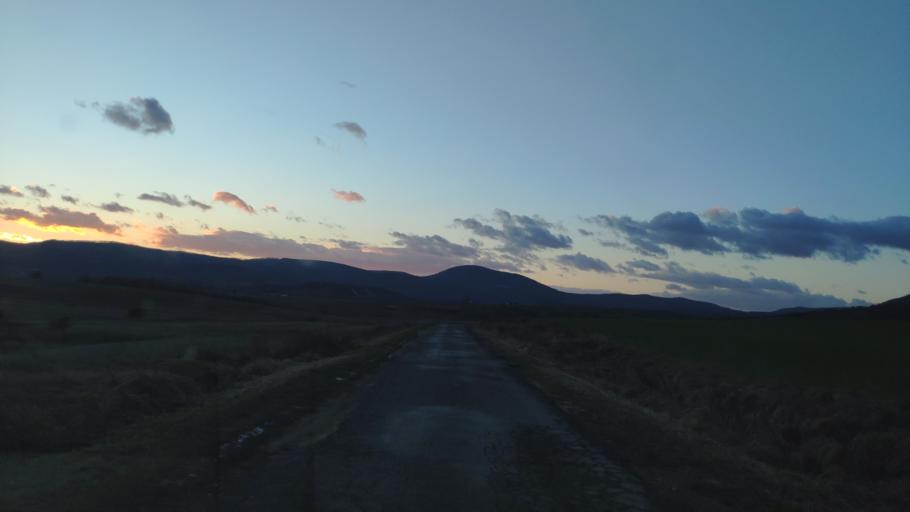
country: HU
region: Borsod-Abauj-Zemplen
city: Olaszliszka
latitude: 48.2665
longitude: 21.3987
